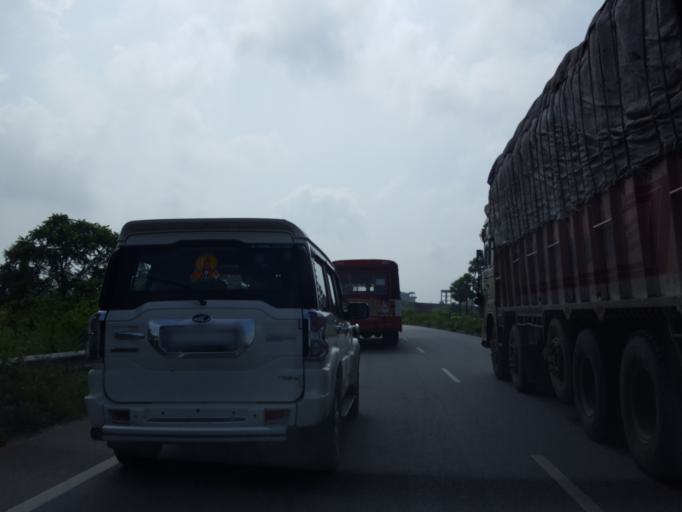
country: IN
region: Telangana
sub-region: Rangareddi
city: Ghatkesar
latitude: 17.2955
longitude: 78.7412
